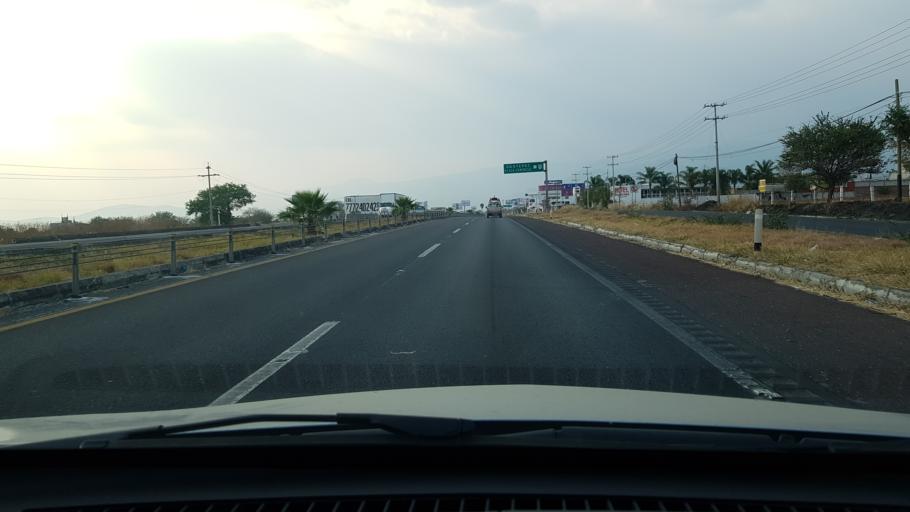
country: MX
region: Morelos
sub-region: Cuautla
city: Tierra Larga (Campo Nuevo)
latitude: 18.8617
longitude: -98.9465
